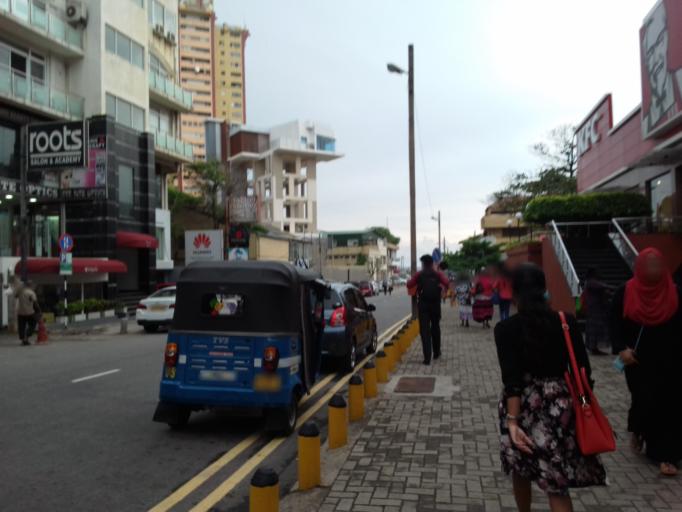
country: LK
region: Western
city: Colombo
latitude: 6.8937
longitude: 79.8547
